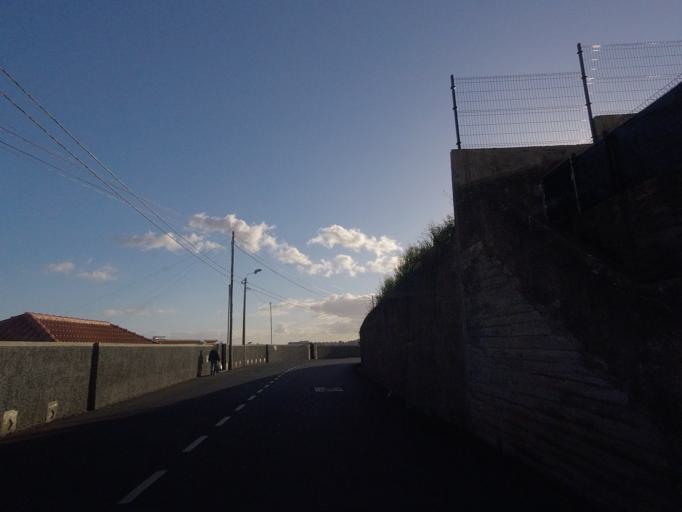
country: PT
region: Madeira
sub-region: Funchal
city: Nossa Senhora do Monte
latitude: 32.6723
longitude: -16.9247
